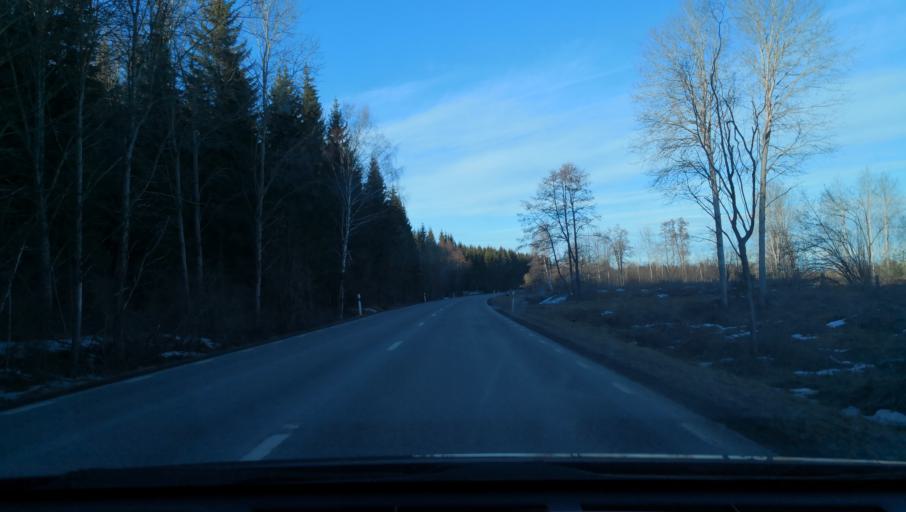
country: SE
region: Uppsala
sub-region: Osthammars Kommun
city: Gimo
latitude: 60.1899
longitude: 18.1900
